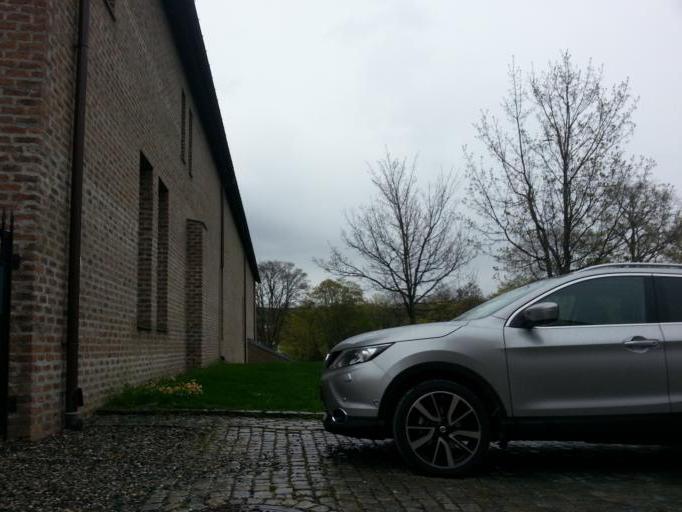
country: NO
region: Sor-Trondelag
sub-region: Trondheim
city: Trondheim
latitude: 63.4257
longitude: 10.3959
